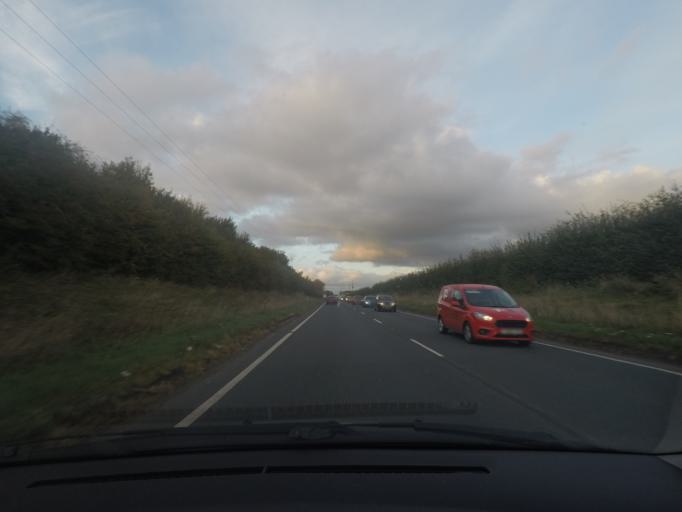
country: GB
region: England
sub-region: City of York
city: Nether Poppleton
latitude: 53.9685
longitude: -1.1463
